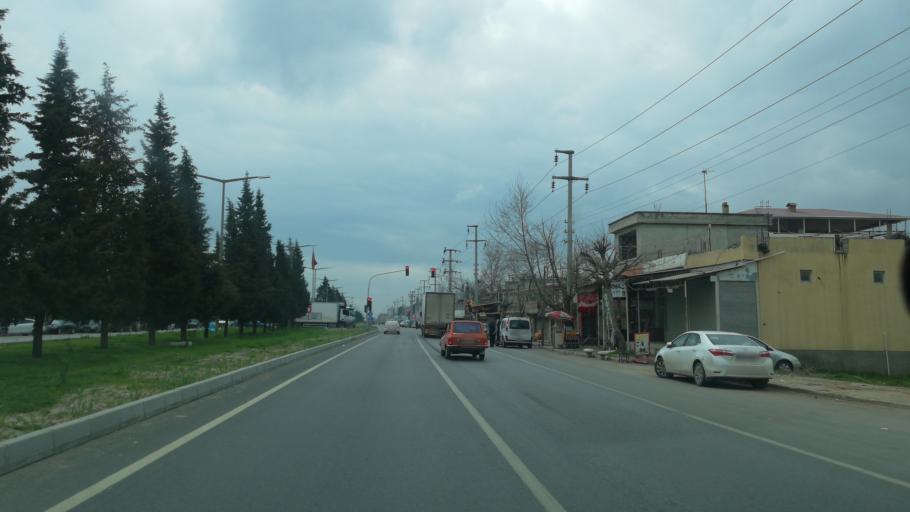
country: TR
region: Kahramanmaras
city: Turkoglu
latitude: 37.4134
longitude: 36.8797
